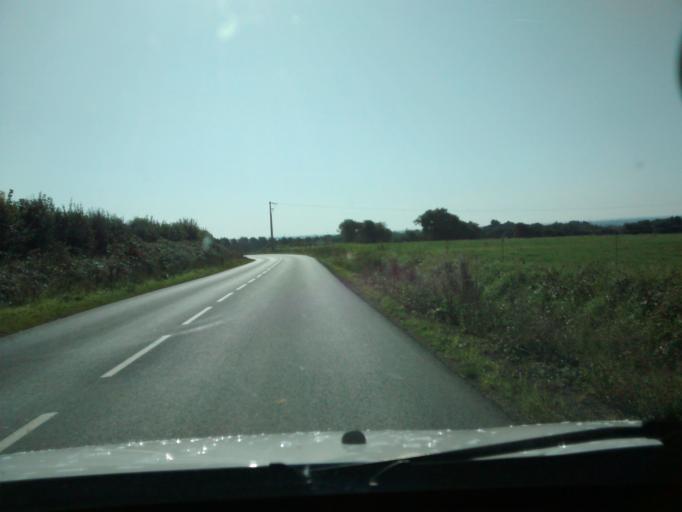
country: FR
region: Brittany
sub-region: Departement des Cotes-d'Armor
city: Penvenan
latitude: 48.7823
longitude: -3.3226
